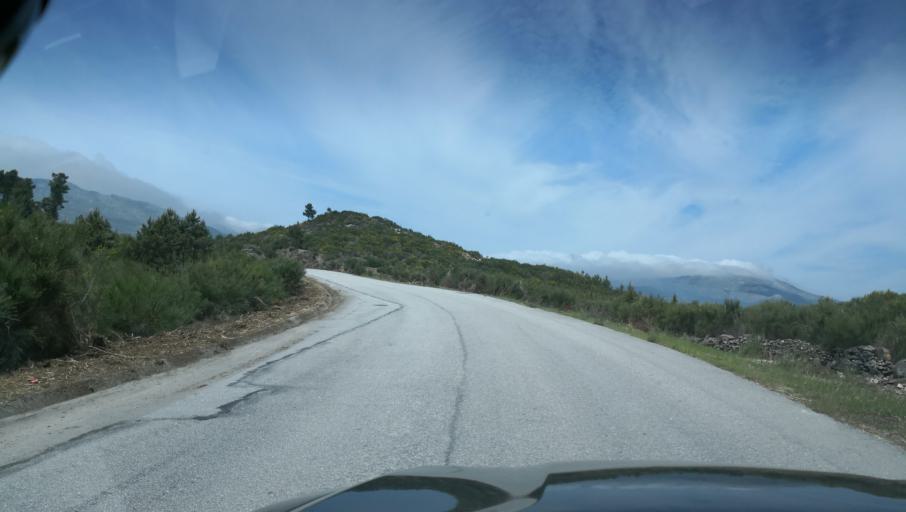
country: PT
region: Vila Real
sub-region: Vila Real
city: Vila Real
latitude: 41.2776
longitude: -7.7998
